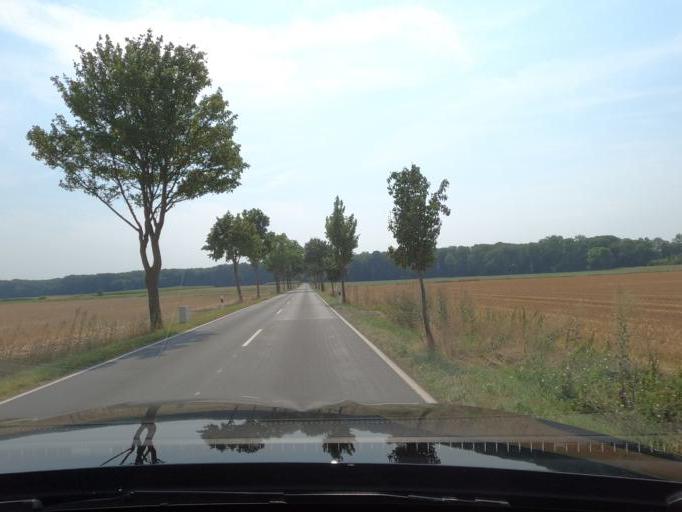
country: DE
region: Lower Saxony
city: Sehnde
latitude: 52.3327
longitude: 9.9169
